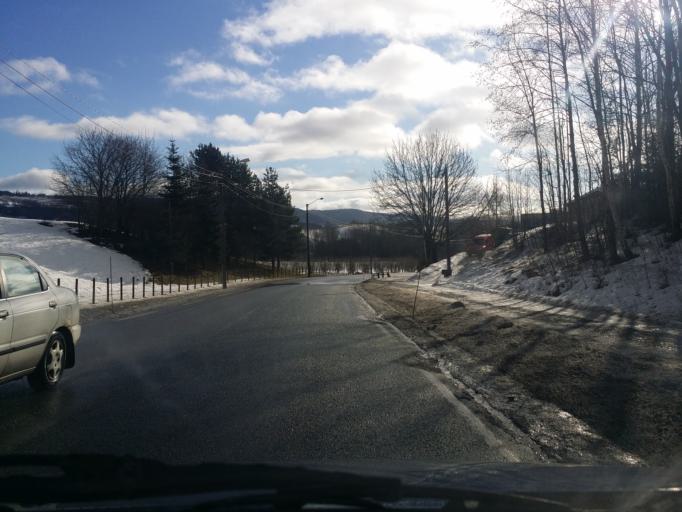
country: NO
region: Buskerud
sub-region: Lier
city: Lierbyen
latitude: 59.8142
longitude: 10.2186
